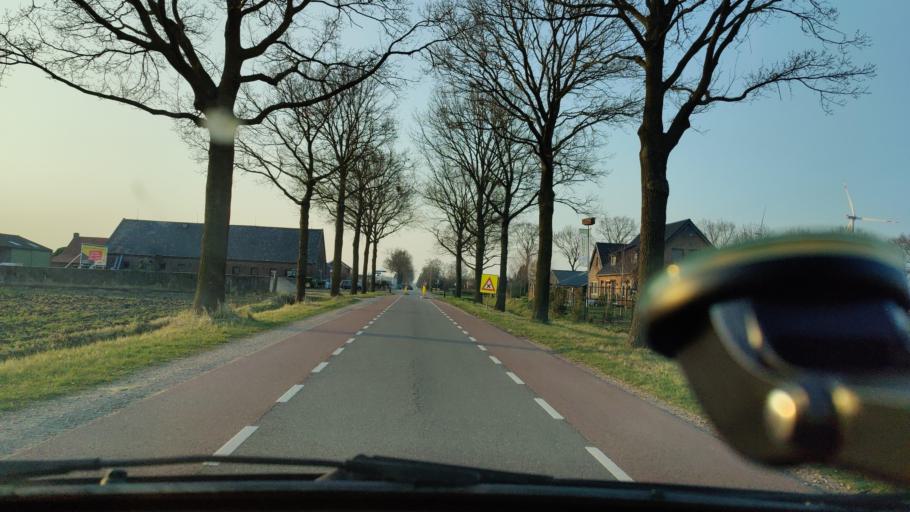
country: NL
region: Limburg
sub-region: Gemeente Bergen
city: Wellerlooi
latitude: 51.5475
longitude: 6.1647
